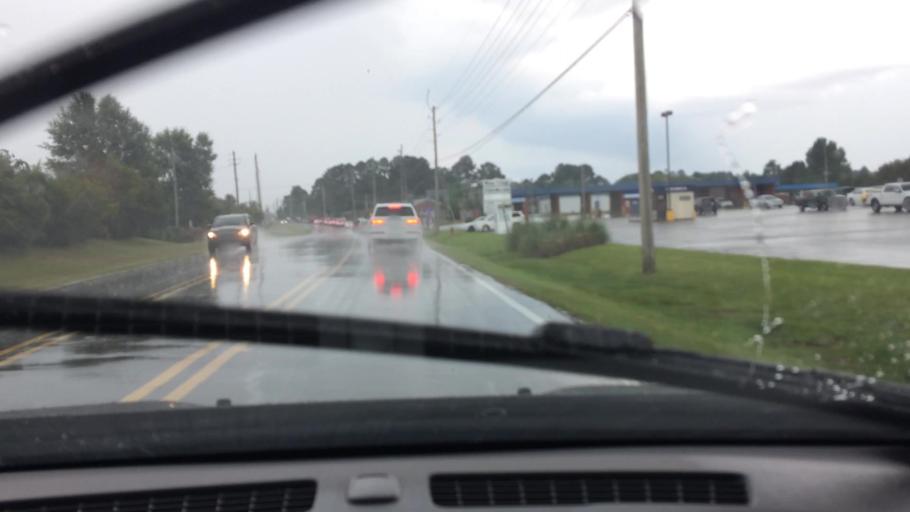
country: US
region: North Carolina
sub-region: Pitt County
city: Winterville
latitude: 35.5312
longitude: -77.3847
